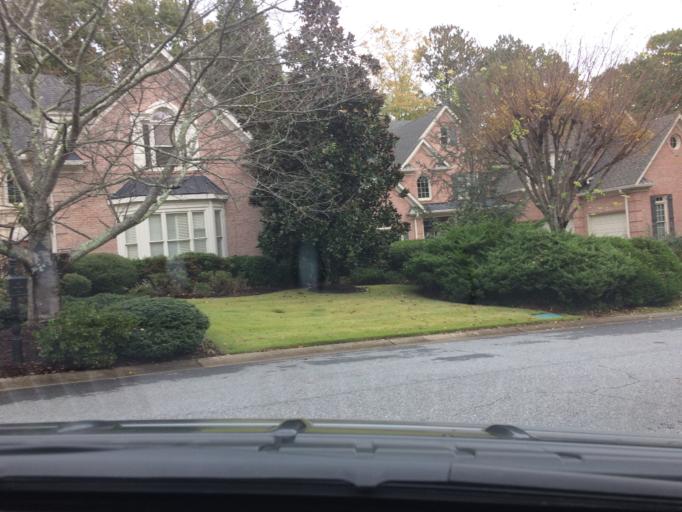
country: US
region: Georgia
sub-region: Fulton County
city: Johns Creek
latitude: 34.0091
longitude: -84.2486
